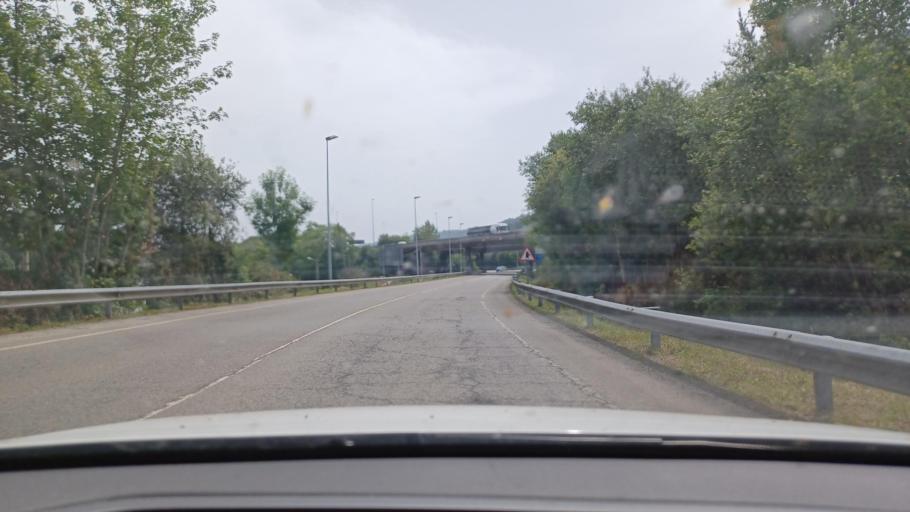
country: ES
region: Asturias
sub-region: Province of Asturias
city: Ribadesella
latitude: 43.4405
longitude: -4.9601
